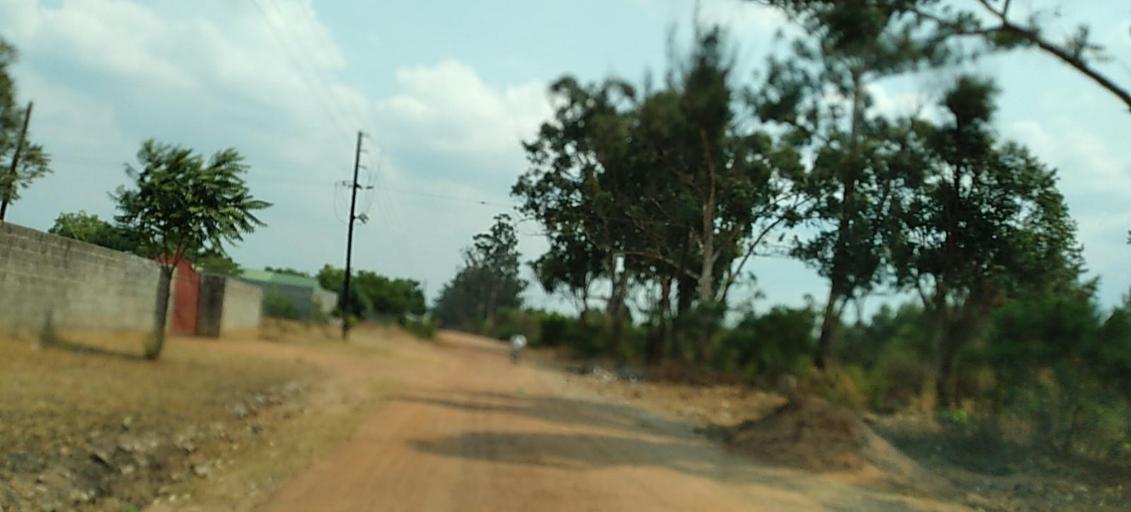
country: ZM
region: Copperbelt
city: Kalulushi
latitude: -12.8405
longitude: 28.0777
